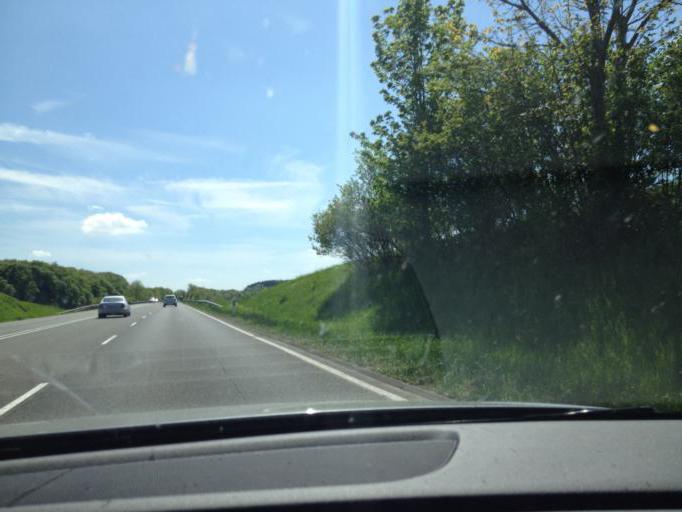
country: DE
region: North Rhine-Westphalia
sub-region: Regierungsbezirk Koln
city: Blankenheim
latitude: 50.4379
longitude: 6.6109
